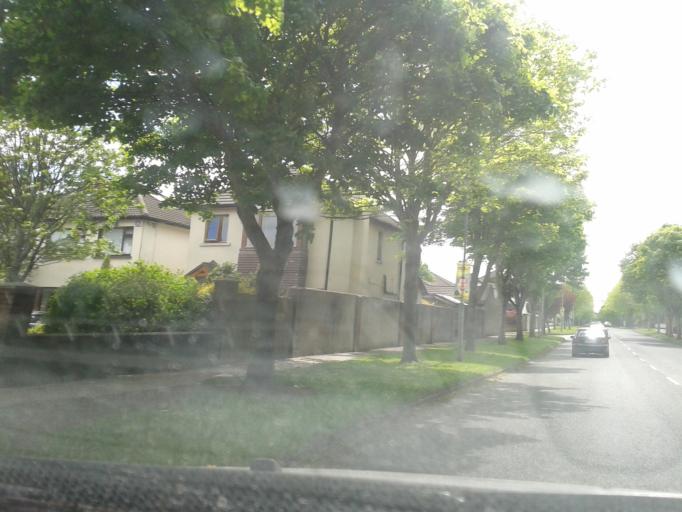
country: IE
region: Leinster
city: Castleknock
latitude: 53.3790
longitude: -6.3586
